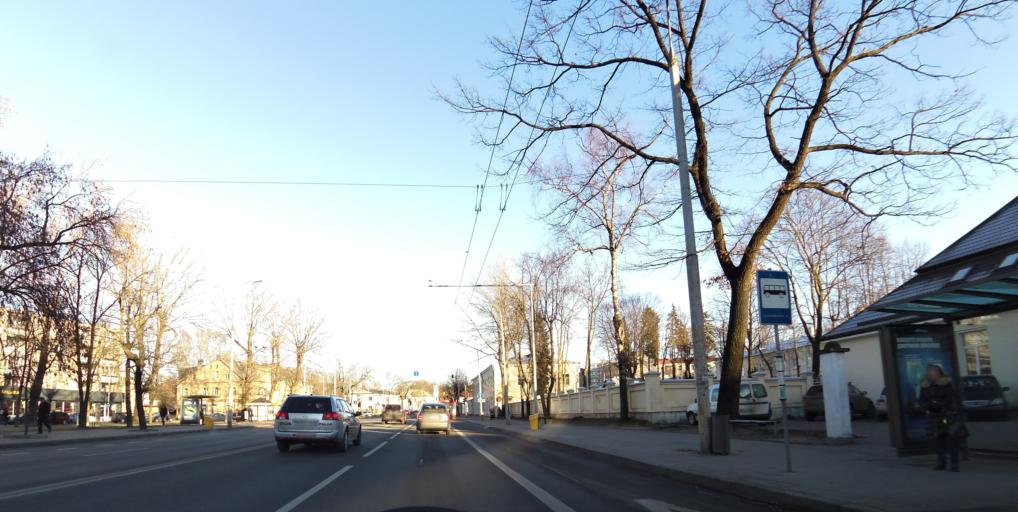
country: LT
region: Vilnius County
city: Naujamiestis
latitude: 54.6794
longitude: 25.2591
